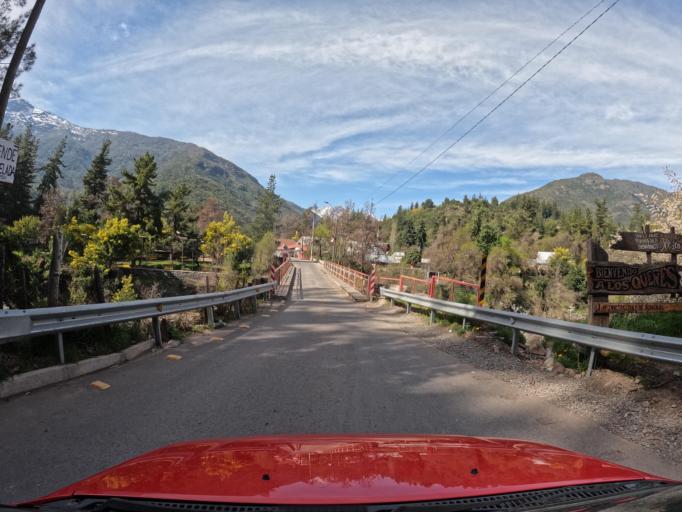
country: CL
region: O'Higgins
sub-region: Provincia de Colchagua
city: Chimbarongo
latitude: -35.0013
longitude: -70.8128
